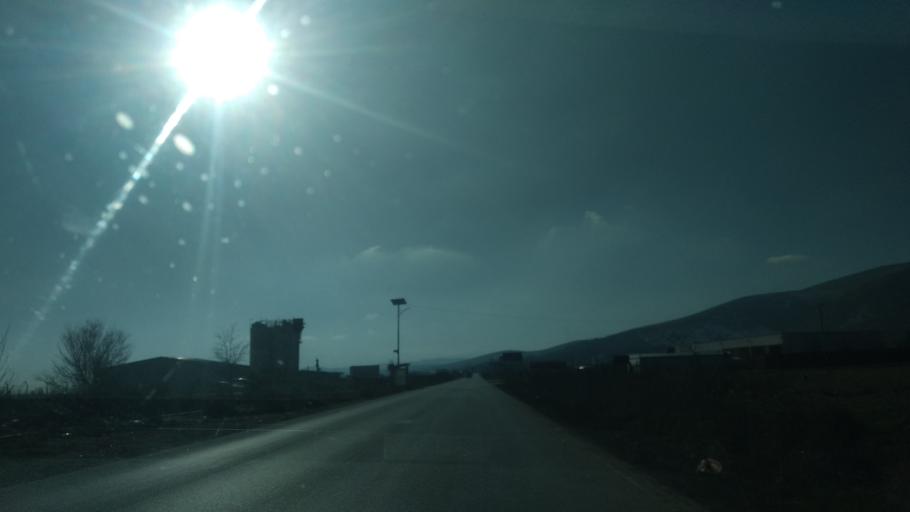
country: XK
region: Pristina
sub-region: Komuna e Gracanices
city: Glanica
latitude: 42.5832
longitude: 21.0156
